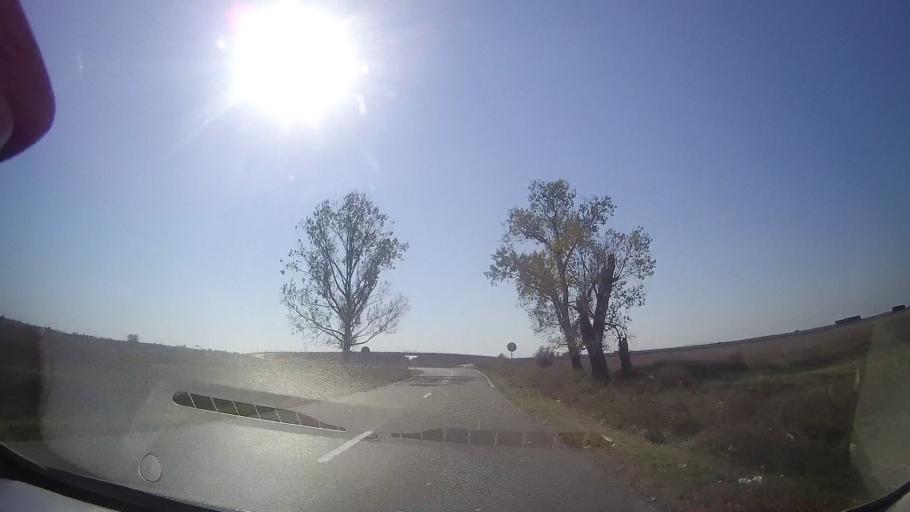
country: RO
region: Timis
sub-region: Comuna Ghizela
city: Ghizela
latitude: 45.7855
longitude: 21.7310
